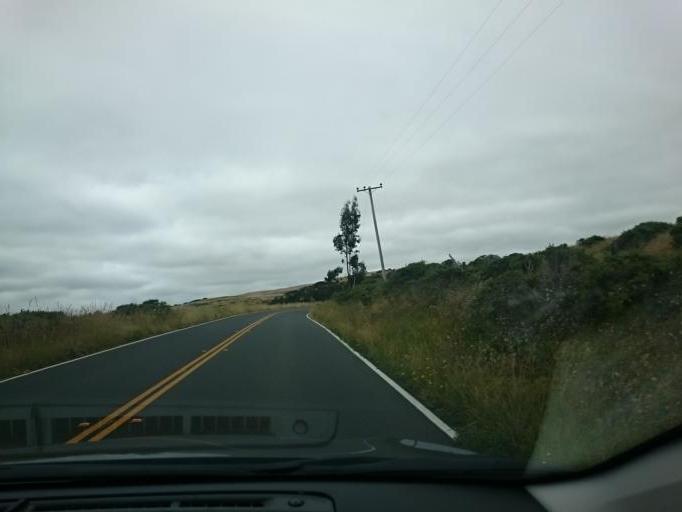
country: US
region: California
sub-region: Marin County
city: Inverness
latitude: 38.1229
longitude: -122.8567
